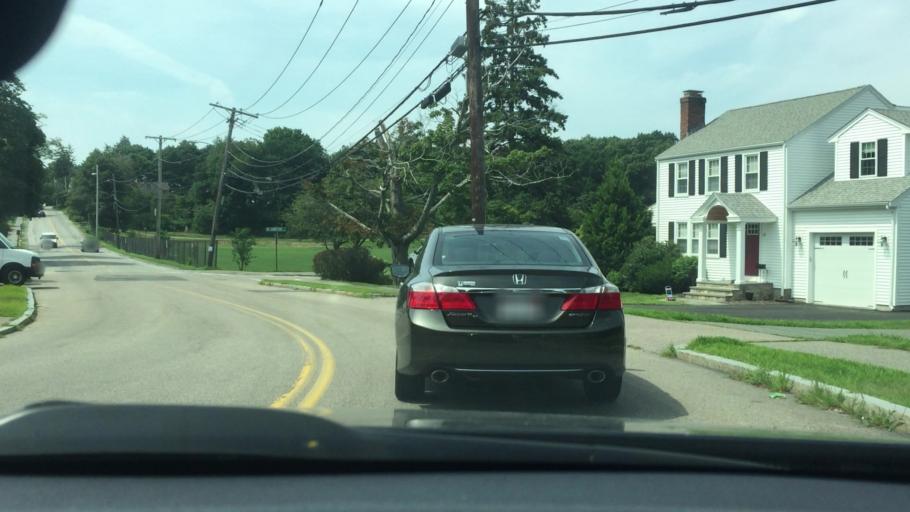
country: US
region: Massachusetts
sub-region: Norfolk County
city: Needham
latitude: 42.3008
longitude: -71.2341
